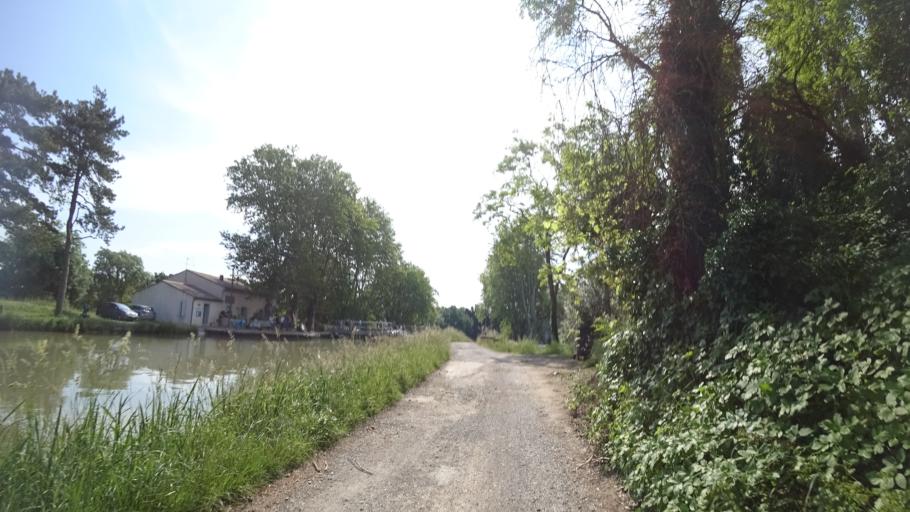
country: FR
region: Languedoc-Roussillon
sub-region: Departement de l'Herault
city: Olonzac
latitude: 43.2697
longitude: 2.7375
